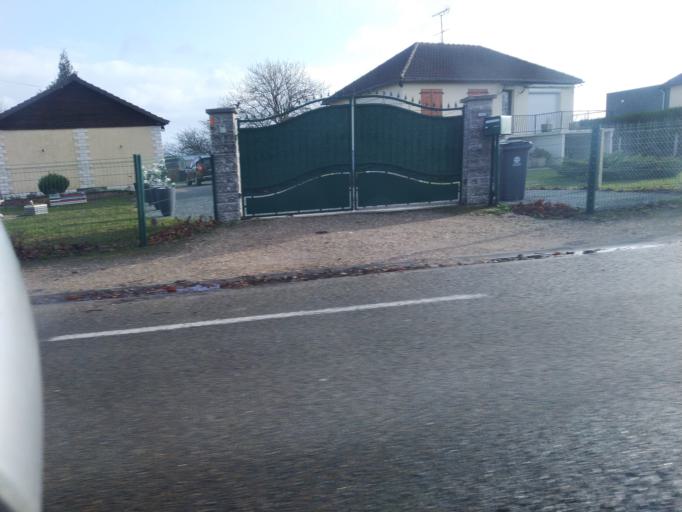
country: FR
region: Haute-Normandie
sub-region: Departement de la Seine-Maritime
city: Jumieges
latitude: 49.4410
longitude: 0.8258
